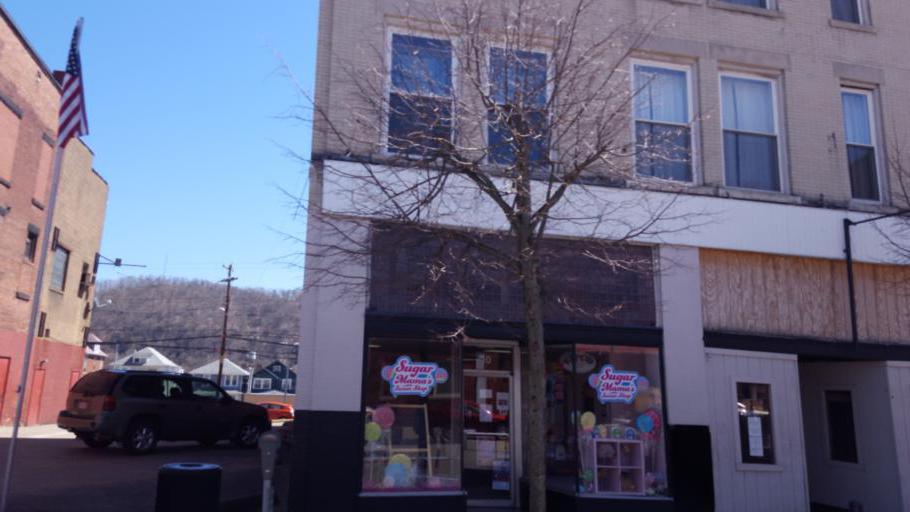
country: US
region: Ohio
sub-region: Belmont County
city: Martins Ferry
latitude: 40.0967
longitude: -80.7231
